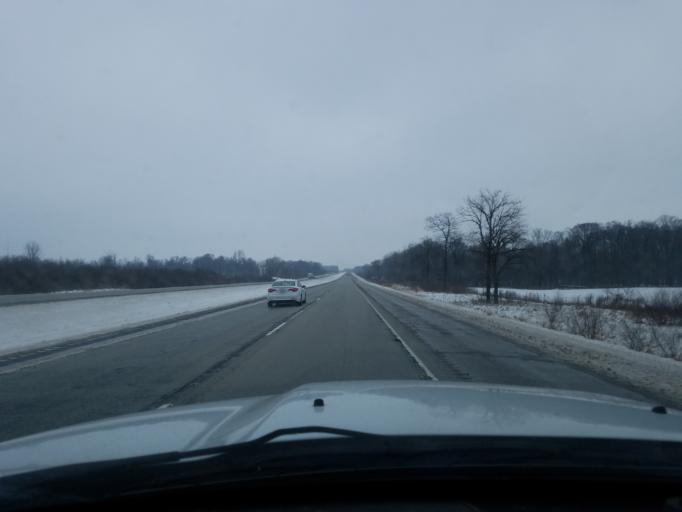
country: US
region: Indiana
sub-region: Fulton County
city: Rochester
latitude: 41.1436
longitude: -86.2396
